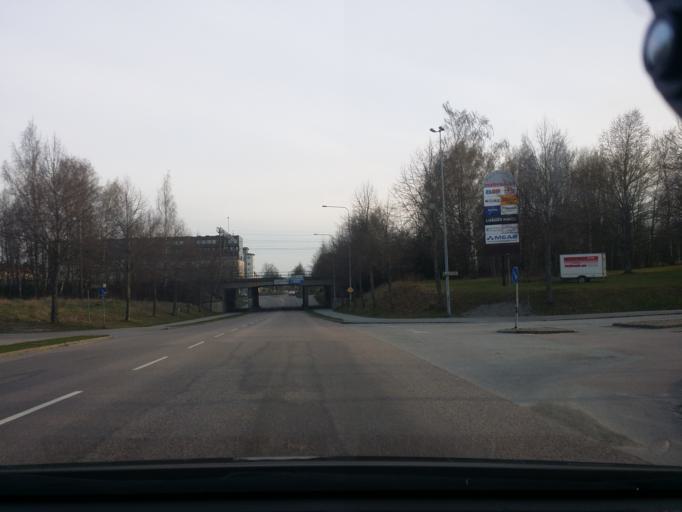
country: SE
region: Uppsala
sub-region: Enkopings Kommun
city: Enkoping
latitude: 59.6466
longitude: 17.0836
